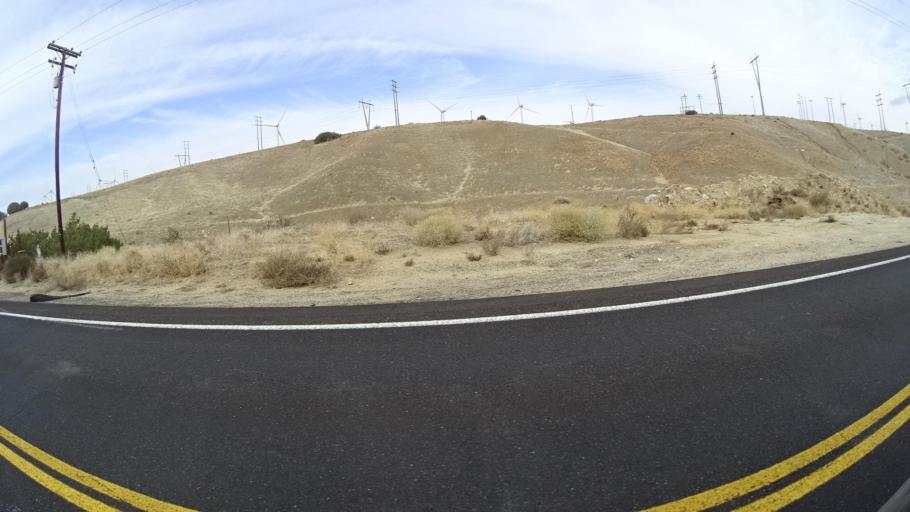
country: US
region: California
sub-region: Kern County
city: Tehachapi
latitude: 35.0513
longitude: -118.3472
